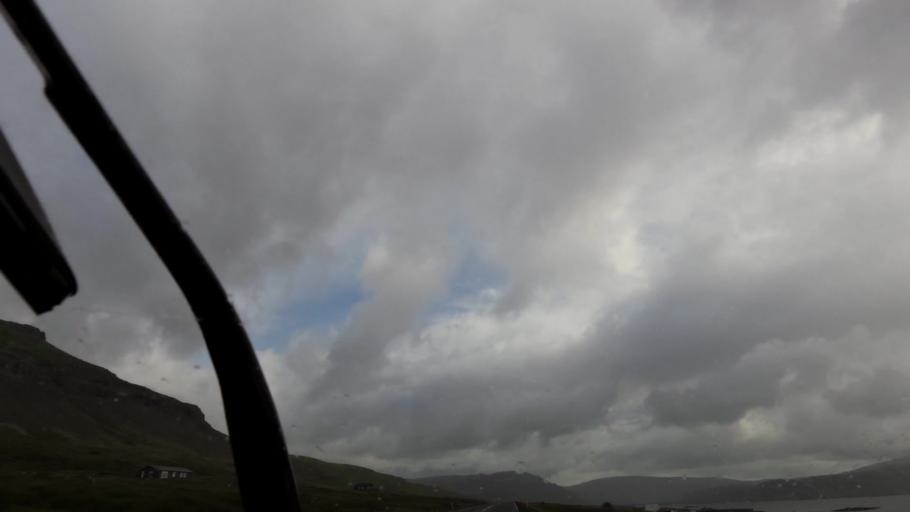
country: IS
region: Westfjords
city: Isafjoerdur
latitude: 65.5486
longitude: -23.2014
